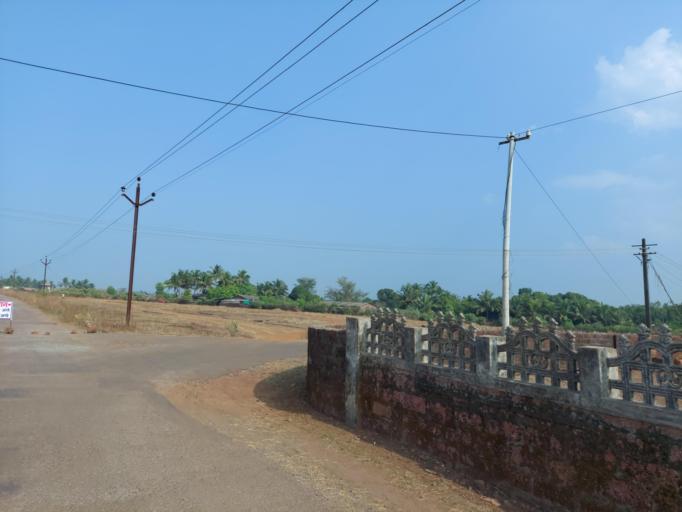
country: IN
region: Maharashtra
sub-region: Ratnagiri
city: Ratnagiri
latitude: 16.9242
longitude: 73.3166
